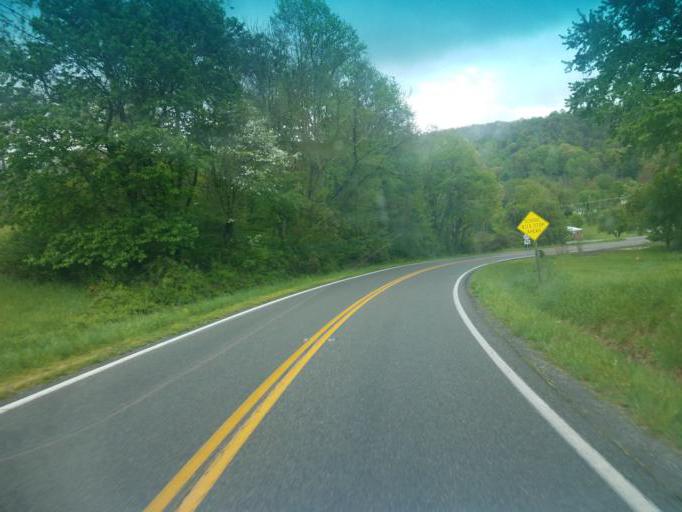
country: US
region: Virginia
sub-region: Washington County
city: Emory
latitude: 36.6486
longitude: -81.7849
